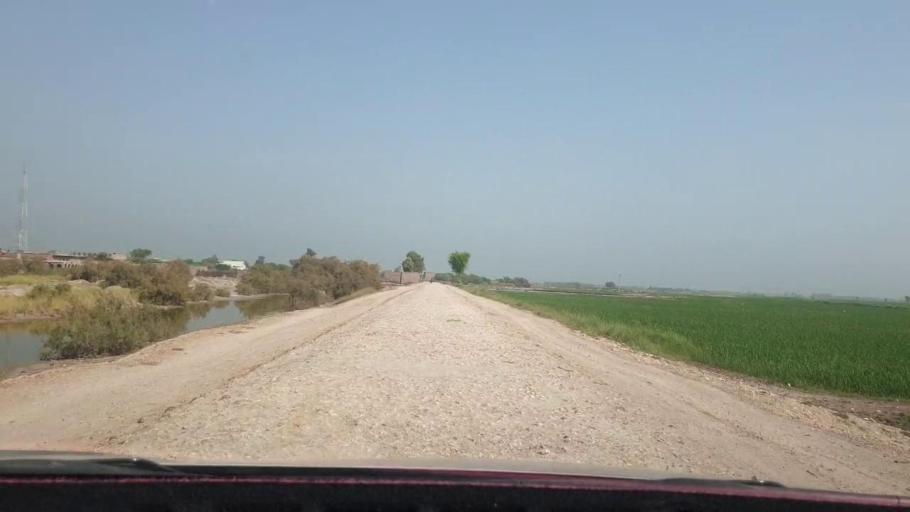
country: PK
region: Sindh
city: Nasirabad
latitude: 27.4216
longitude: 67.9285
